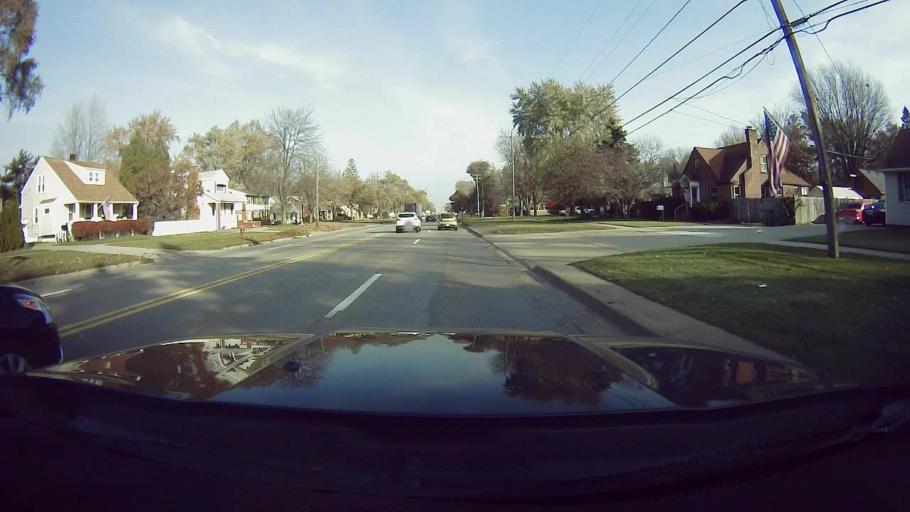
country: US
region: Michigan
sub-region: Oakland County
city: Clawson
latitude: 42.5336
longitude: -83.1342
